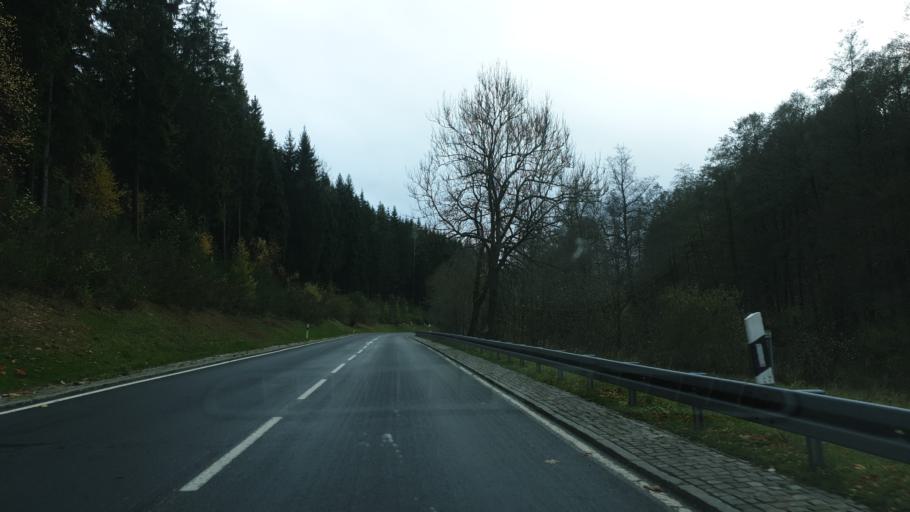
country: DE
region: Saxony
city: Schoenheide
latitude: 50.5020
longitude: 12.5533
